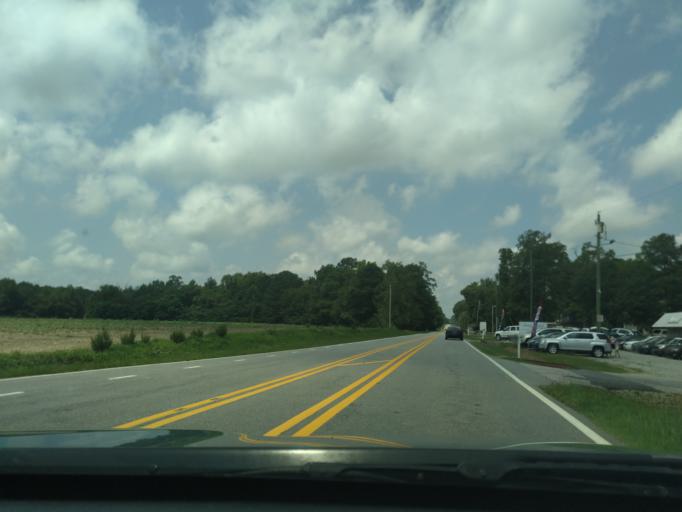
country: US
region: North Carolina
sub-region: Nash County
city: Red Oak
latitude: 36.0013
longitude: -77.8394
